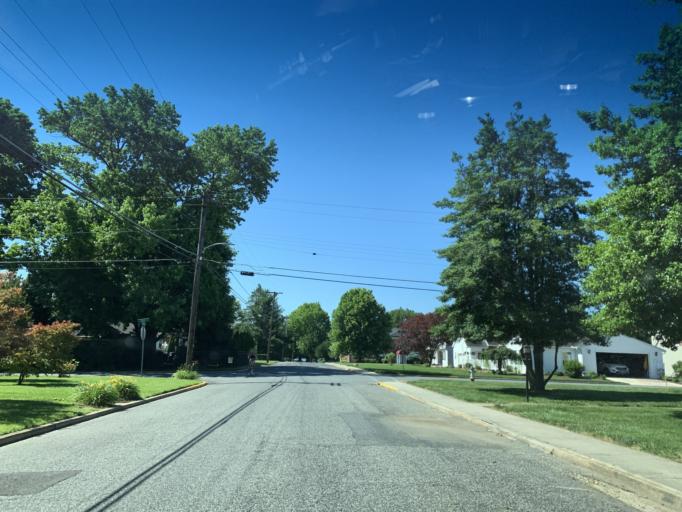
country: US
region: Maryland
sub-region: Harford County
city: Havre de Grace
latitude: 39.5399
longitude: -76.0950
